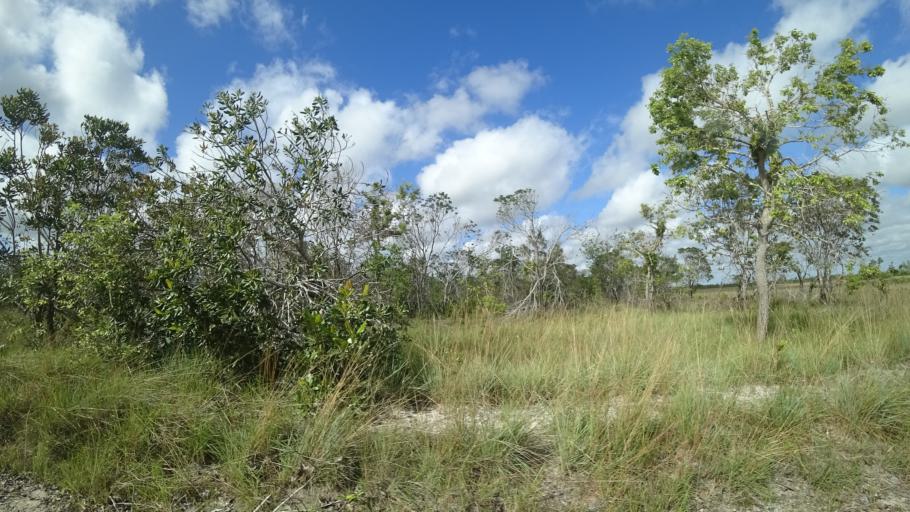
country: MZ
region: Sofala
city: Beira
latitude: -19.6128
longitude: 35.0746
